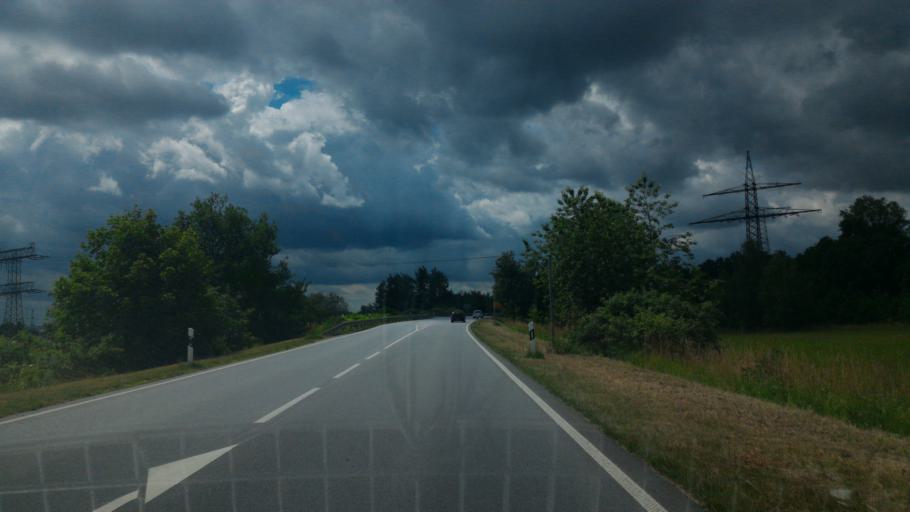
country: DE
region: Saxony
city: Ostritz
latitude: 51.0633
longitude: 14.9577
